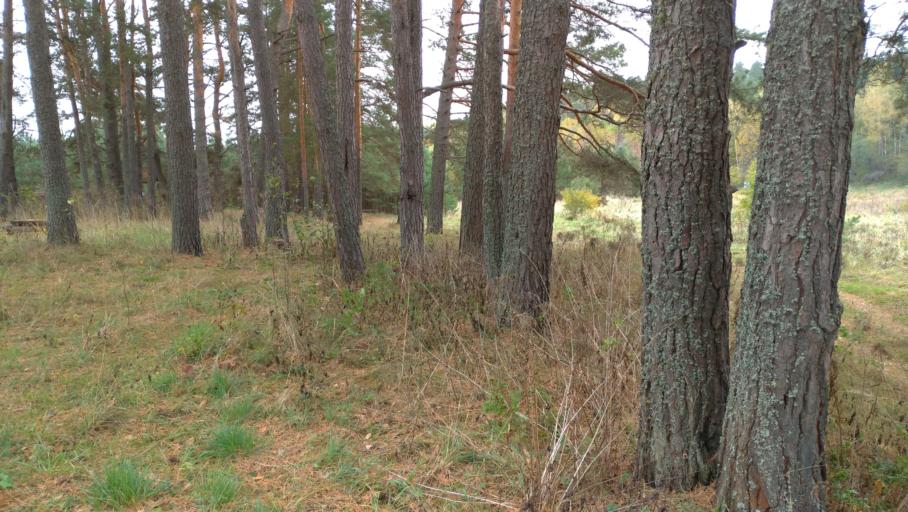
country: RU
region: Kaluga
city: Yukhnov
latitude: 54.7698
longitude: 35.0620
